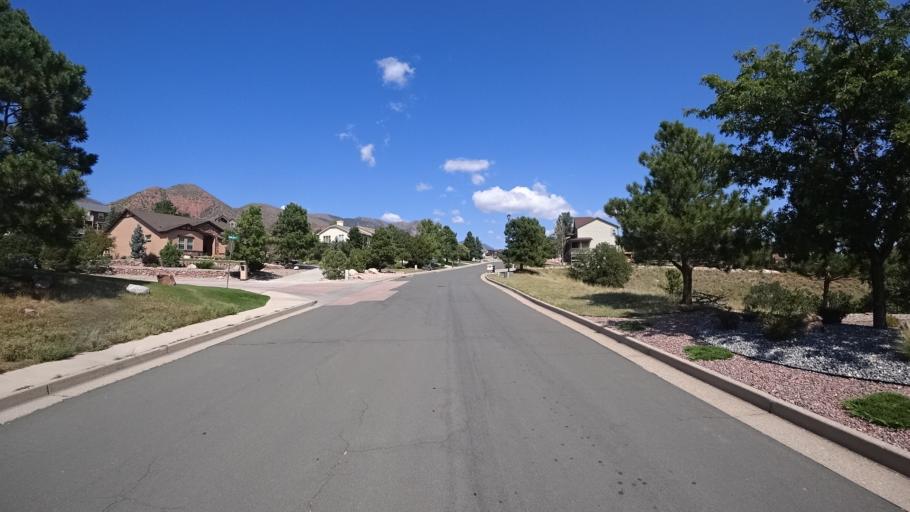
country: US
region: Colorado
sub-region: El Paso County
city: Manitou Springs
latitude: 38.9197
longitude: -104.8745
